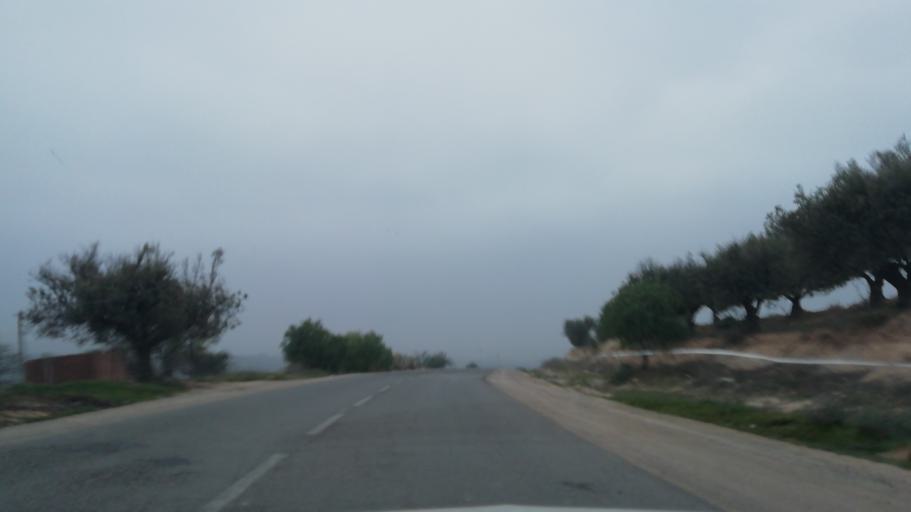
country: DZ
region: Mascara
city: Mascara
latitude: 35.3967
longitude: 0.1652
